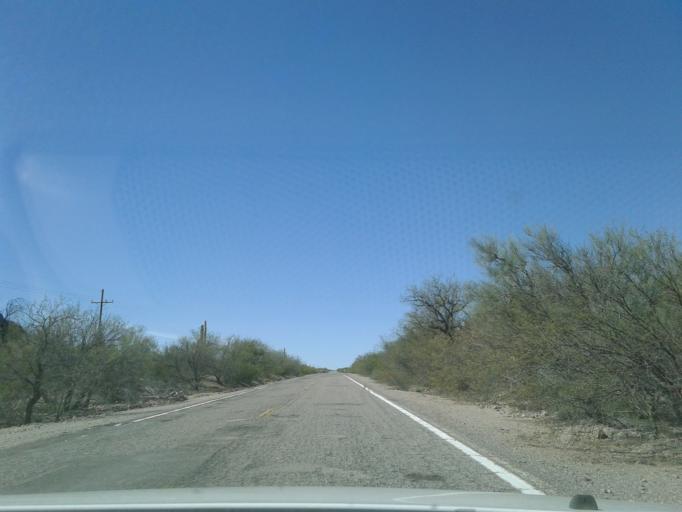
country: US
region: Arizona
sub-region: Pima County
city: Avra Valley
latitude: 32.3755
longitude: -111.4670
